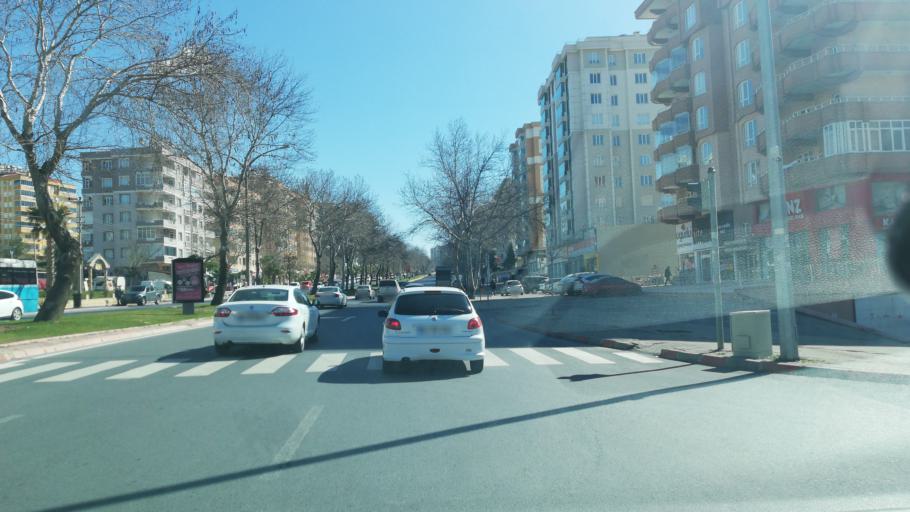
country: TR
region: Kahramanmaras
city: Kahramanmaras
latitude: 37.5914
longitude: 36.8682
